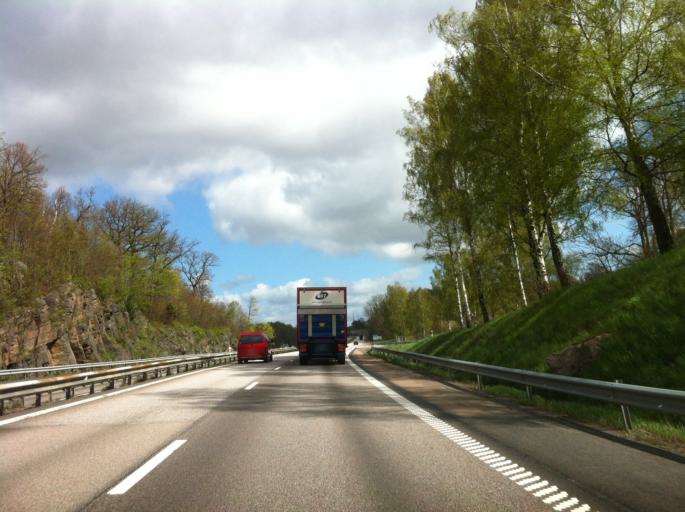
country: SE
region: Vaestra Goetaland
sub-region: Alingsas Kommun
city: Ingared
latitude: 57.8963
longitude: 12.4893
